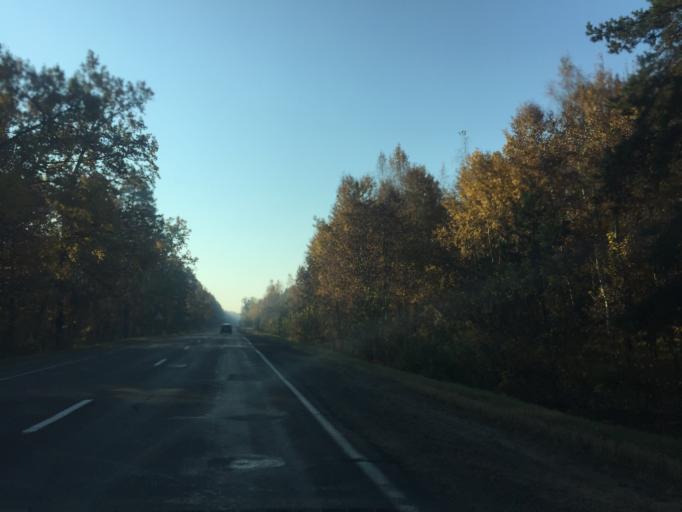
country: BY
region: Gomel
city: Gomel
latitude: 52.4096
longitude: 30.8288
